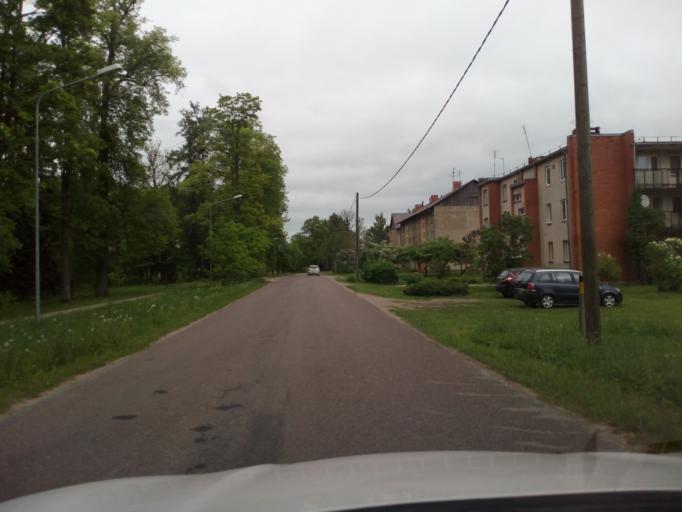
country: LV
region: Krimulda
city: Ragana
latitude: 57.3430
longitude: 24.6623
